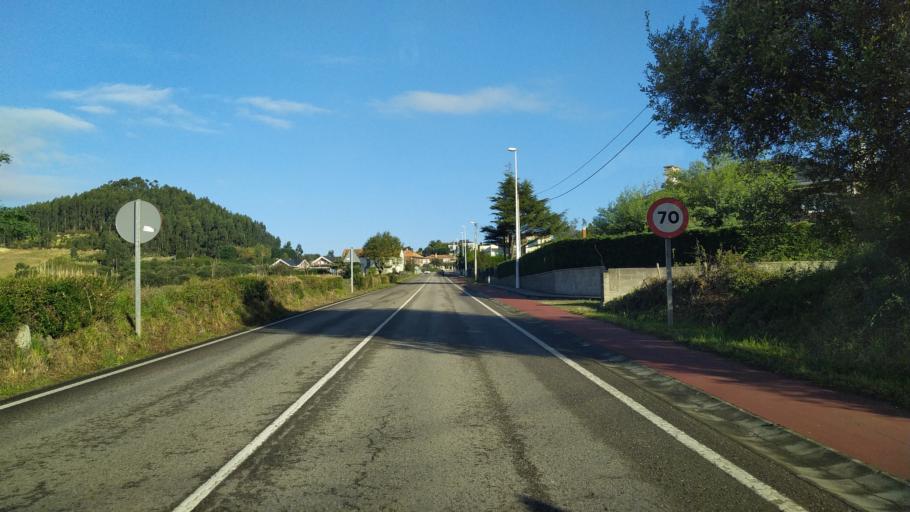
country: ES
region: Cantabria
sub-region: Provincia de Cantabria
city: Santa Cruz de Bezana
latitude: 43.4359
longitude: -3.9190
